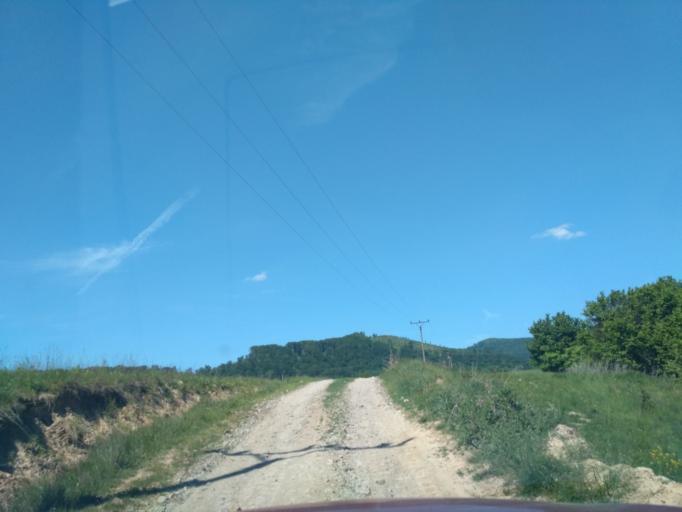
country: SK
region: Presovsky
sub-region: Okres Presov
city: Presov
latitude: 48.8914
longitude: 21.3921
